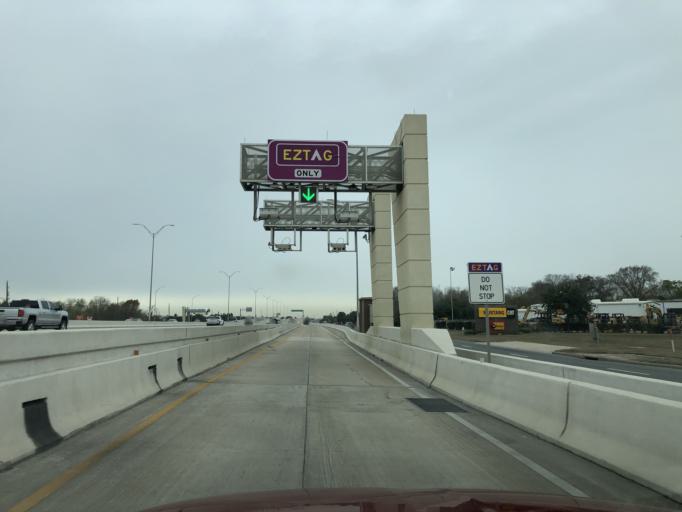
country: US
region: Texas
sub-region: Fort Bend County
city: Missouri City
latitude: 29.6330
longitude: -95.5255
